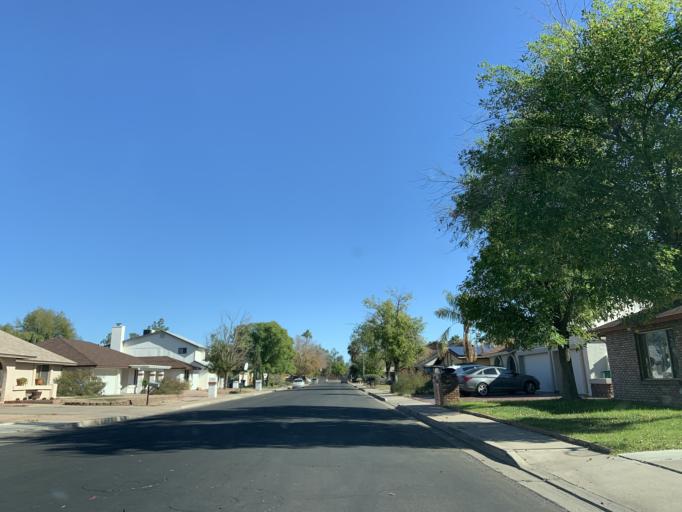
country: US
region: Arizona
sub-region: Maricopa County
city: San Carlos
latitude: 33.3701
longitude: -111.8565
